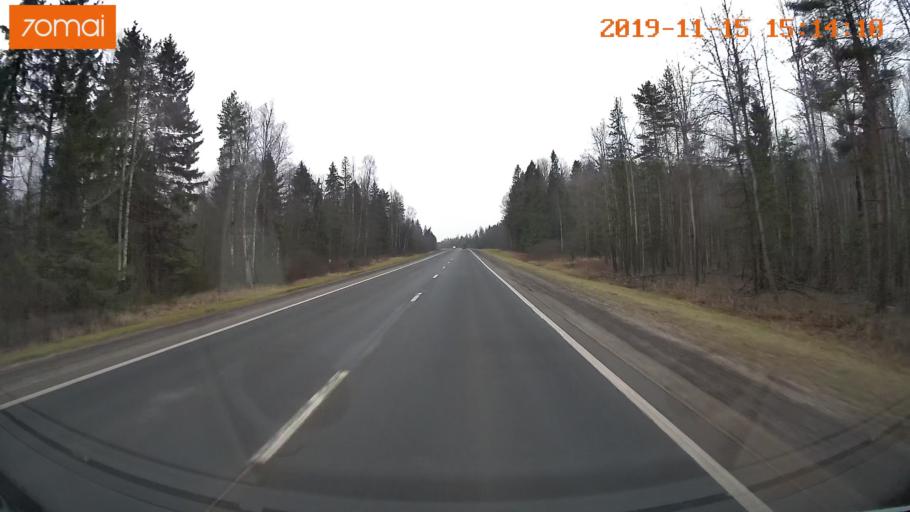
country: RU
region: Jaroslavl
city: Danilov
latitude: 58.3037
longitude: 40.2088
